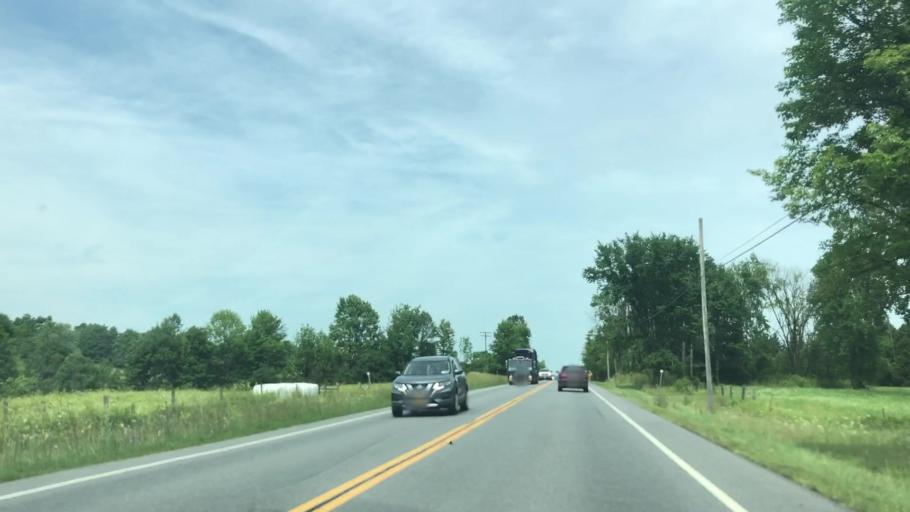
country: US
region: New York
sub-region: Washington County
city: Whitehall
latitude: 43.5078
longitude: -73.4190
